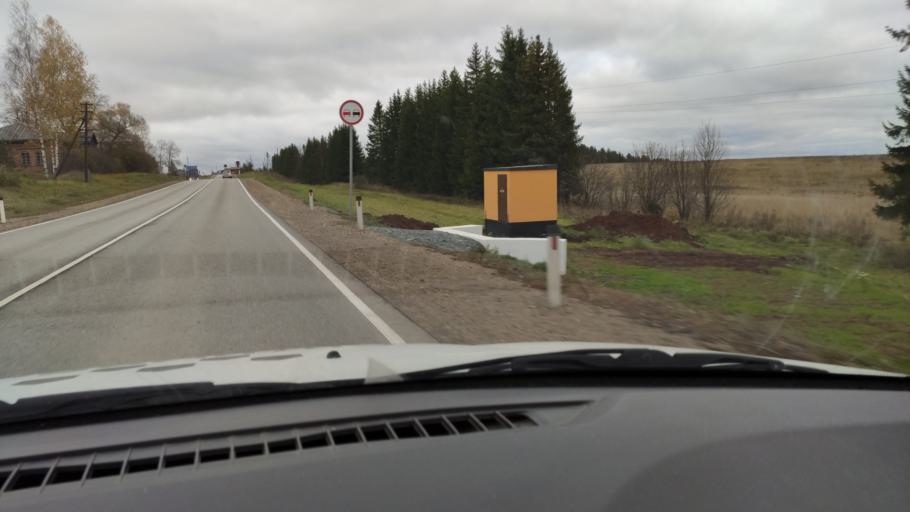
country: RU
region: Kirov
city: Slobodskoy
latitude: 58.7480
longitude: 50.3096
